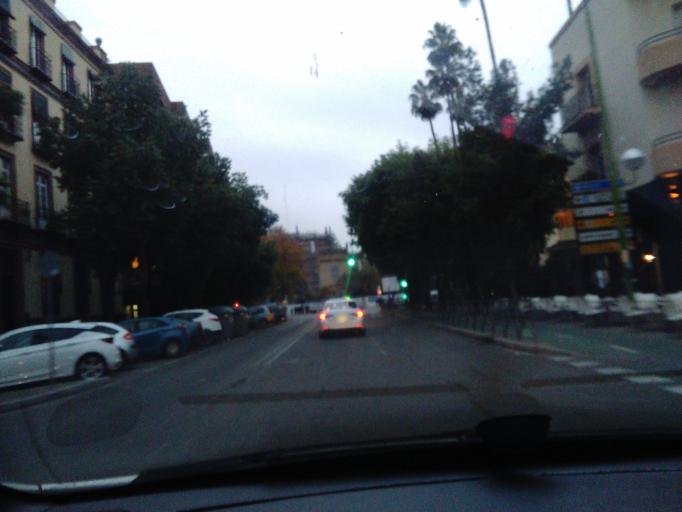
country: ES
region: Andalusia
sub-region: Provincia de Sevilla
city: Sevilla
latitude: 37.3719
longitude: -5.9844
